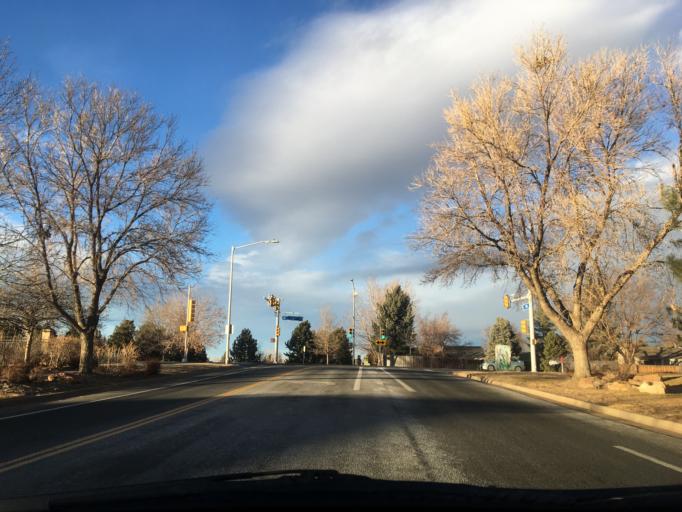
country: US
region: Colorado
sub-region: Broomfield County
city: Broomfield
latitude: 39.9428
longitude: -105.0720
